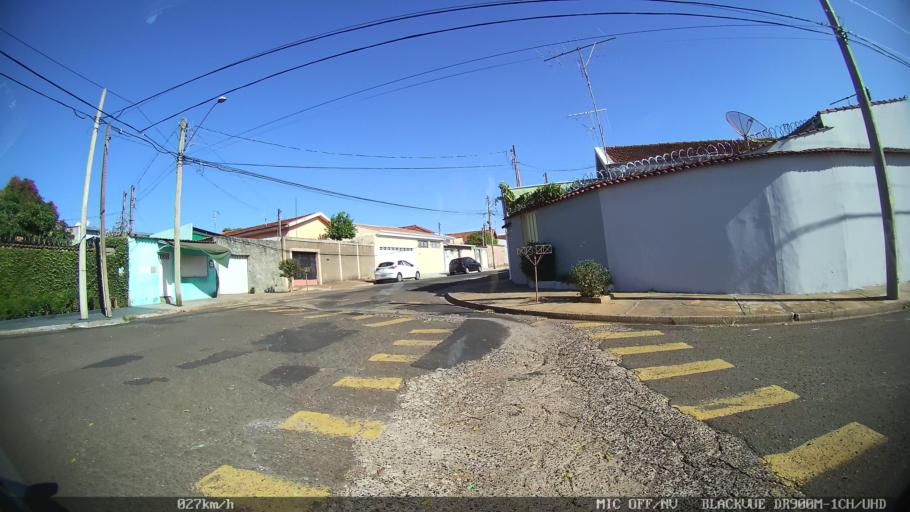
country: BR
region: Sao Paulo
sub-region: Franca
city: Franca
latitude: -20.4941
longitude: -47.4219
